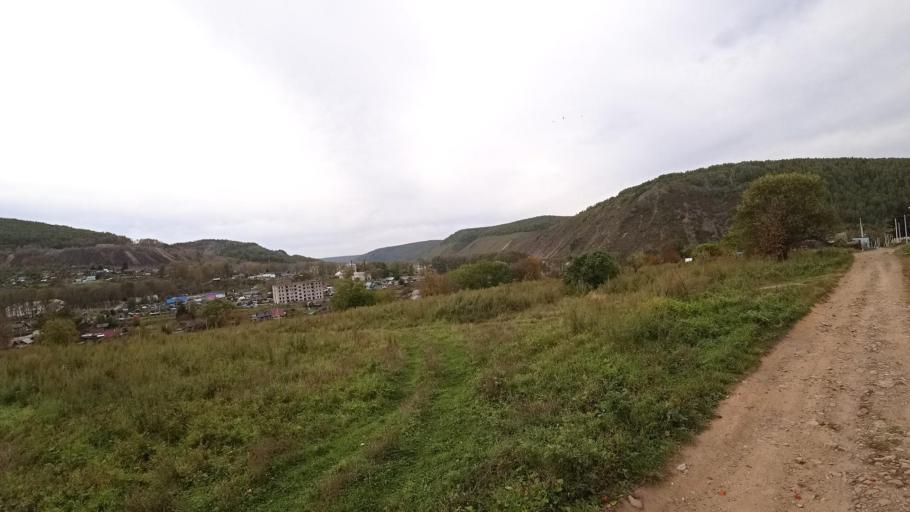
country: RU
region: Jewish Autonomous Oblast
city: Khingansk
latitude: 49.1283
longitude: 131.2028
